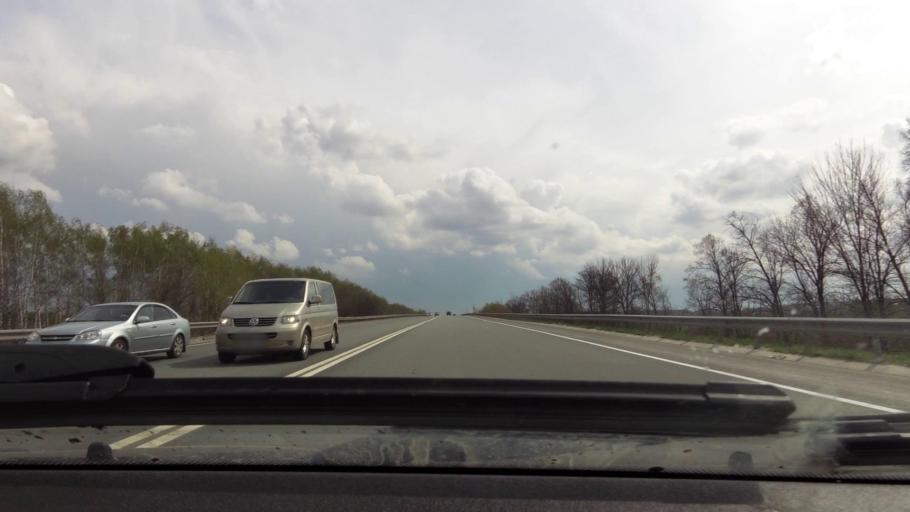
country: RU
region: Rjazan
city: Bagramovo
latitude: 54.7386
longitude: 39.4477
